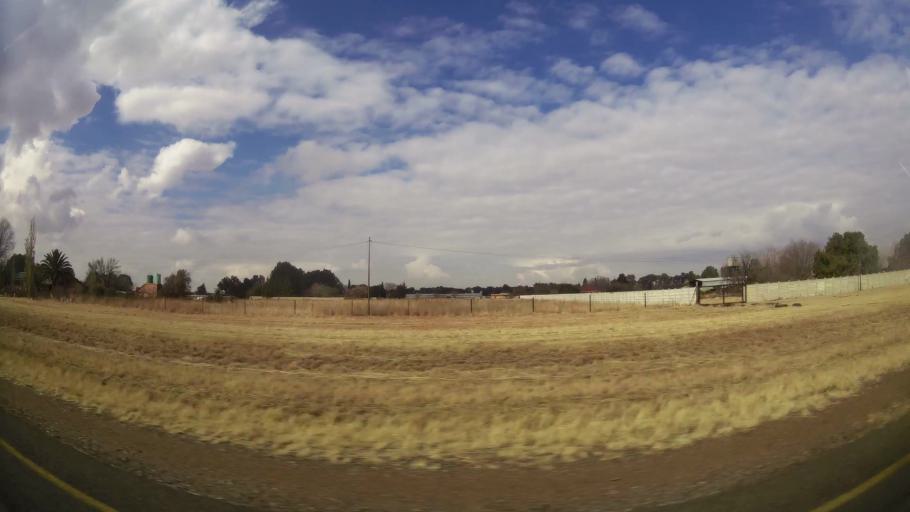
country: ZA
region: Gauteng
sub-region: Sedibeng District Municipality
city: Meyerton
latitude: -26.6398
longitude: 28.0479
